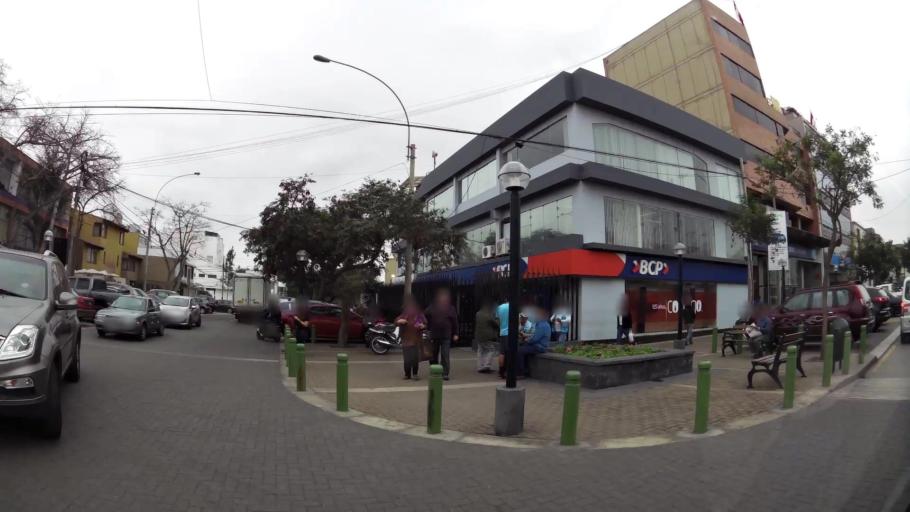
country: PE
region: Lima
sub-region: Lima
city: Surco
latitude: -12.1221
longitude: -77.0116
